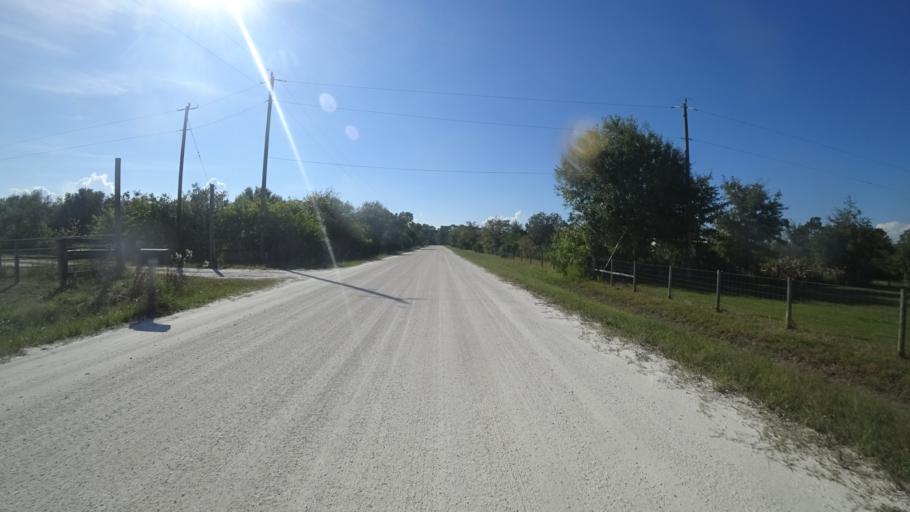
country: US
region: Florida
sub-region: Sarasota County
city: The Meadows
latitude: 27.4227
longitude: -82.2682
